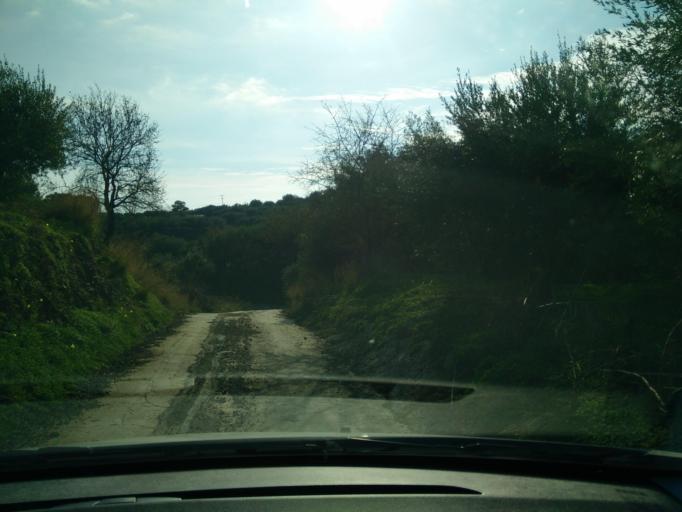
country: GR
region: Crete
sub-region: Nomos Lasithiou
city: Gra Liyia
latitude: 35.0282
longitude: 25.5692
